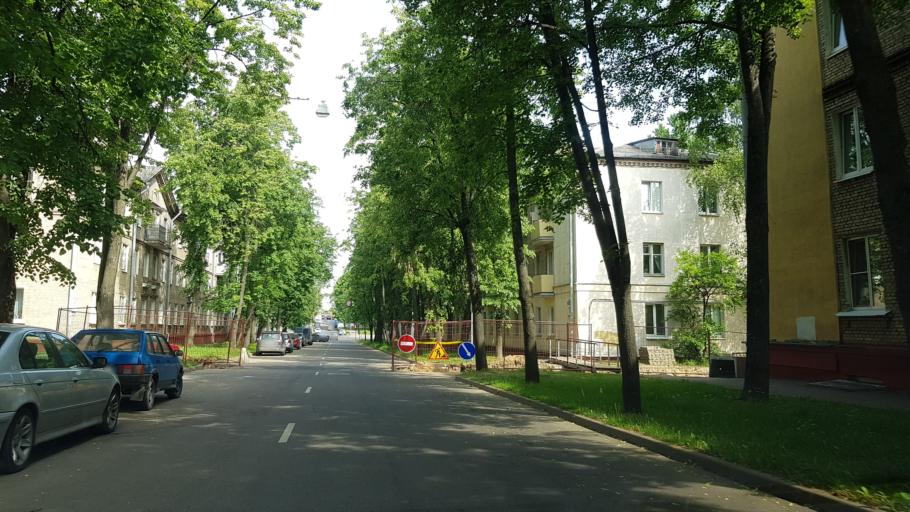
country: BY
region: Minsk
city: Minsk
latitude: 53.8927
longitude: 27.5229
